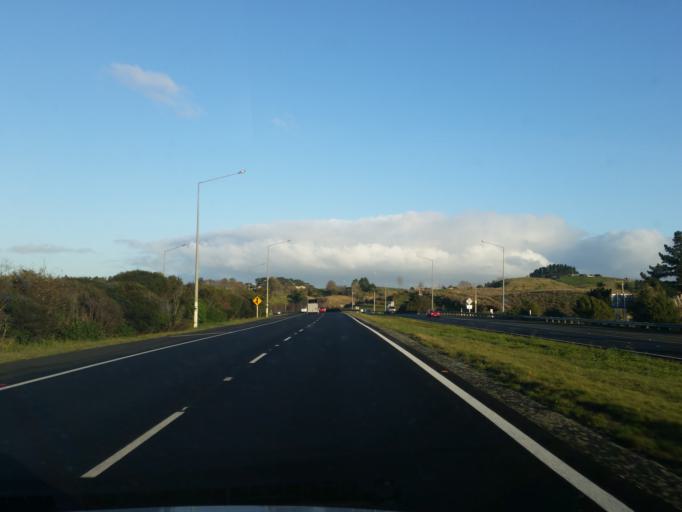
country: NZ
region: Auckland
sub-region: Auckland
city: Pukekohe East
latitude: -37.2490
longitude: 175.0285
